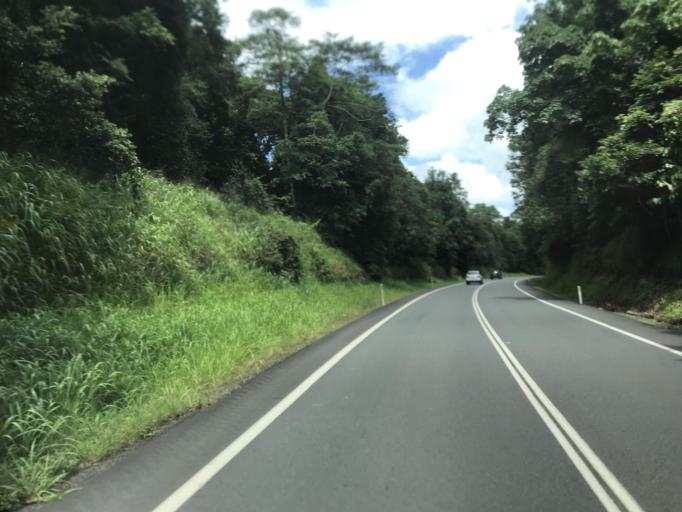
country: AU
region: Queensland
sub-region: Cassowary Coast
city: Innisfail
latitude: -17.6096
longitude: 145.7838
